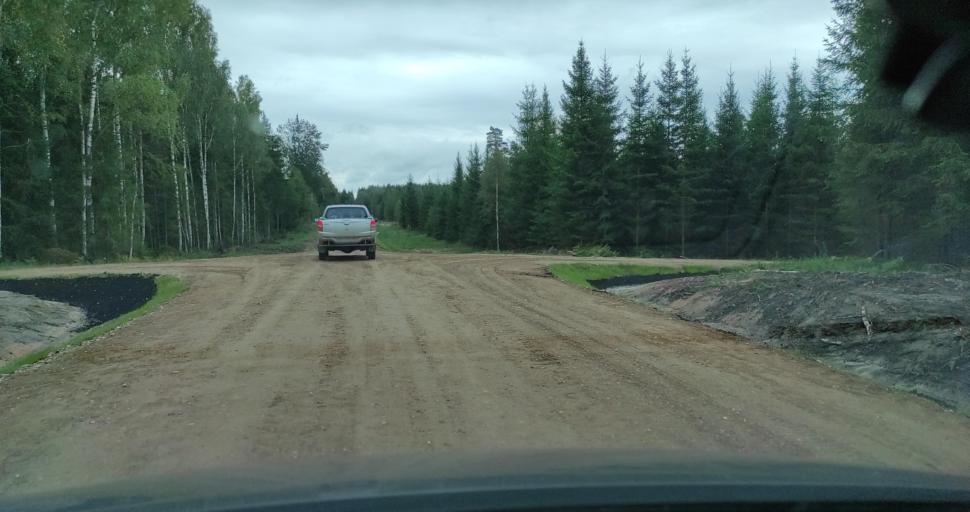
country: LV
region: Talsu Rajons
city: Sabile
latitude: 57.0188
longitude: 22.3534
